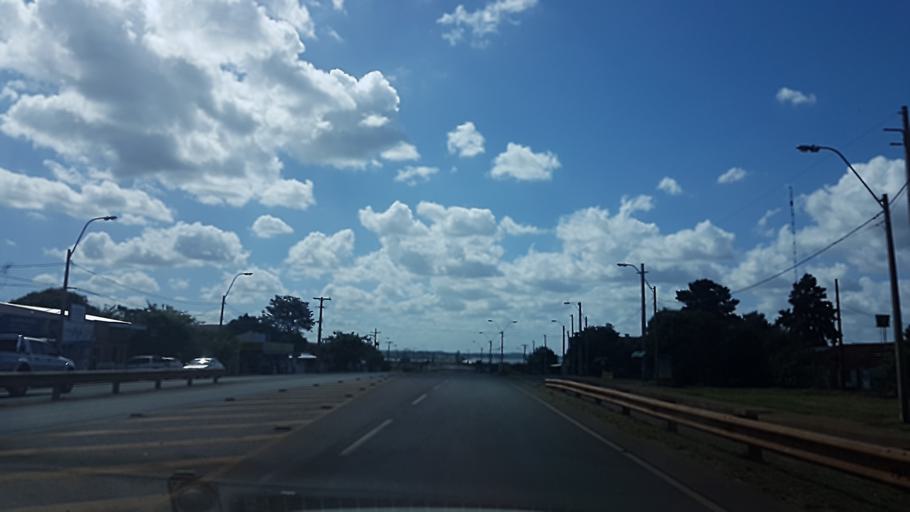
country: PY
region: Itapua
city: Carmen del Parana
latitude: -27.2185
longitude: -56.1445
